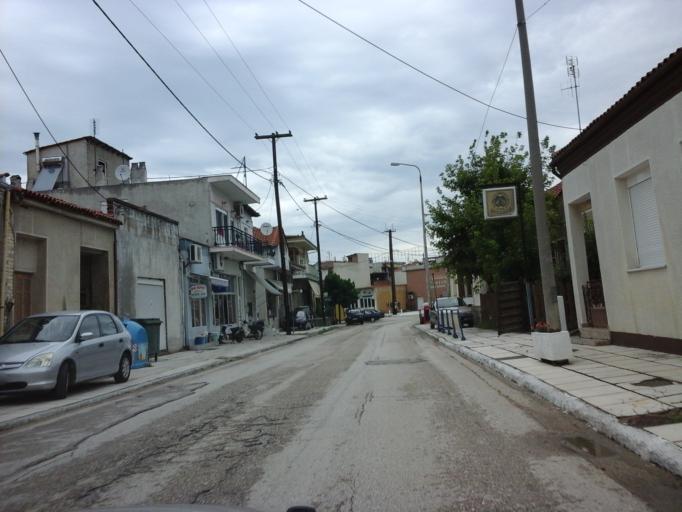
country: GR
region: East Macedonia and Thrace
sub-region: Nomos Evrou
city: Soufli
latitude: 41.1891
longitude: 26.3009
